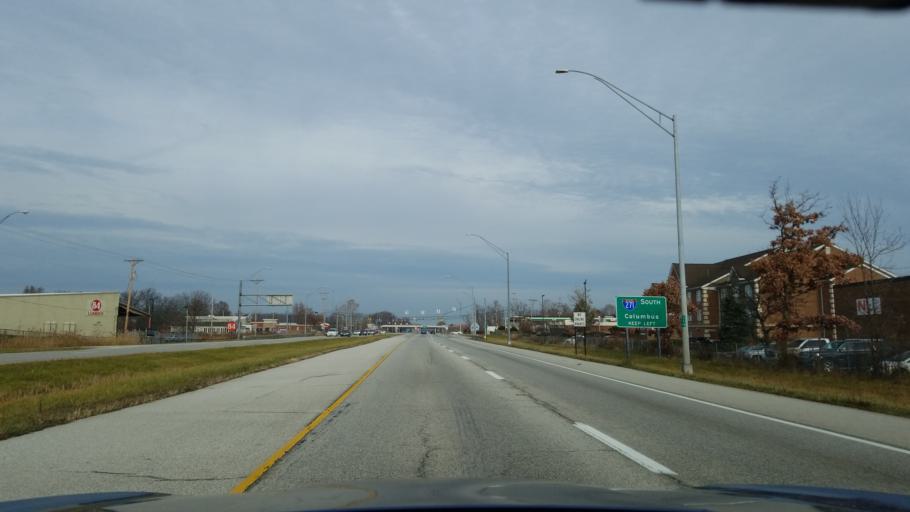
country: US
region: Ohio
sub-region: Summit County
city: Macedonia
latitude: 41.2969
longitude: -81.5136
